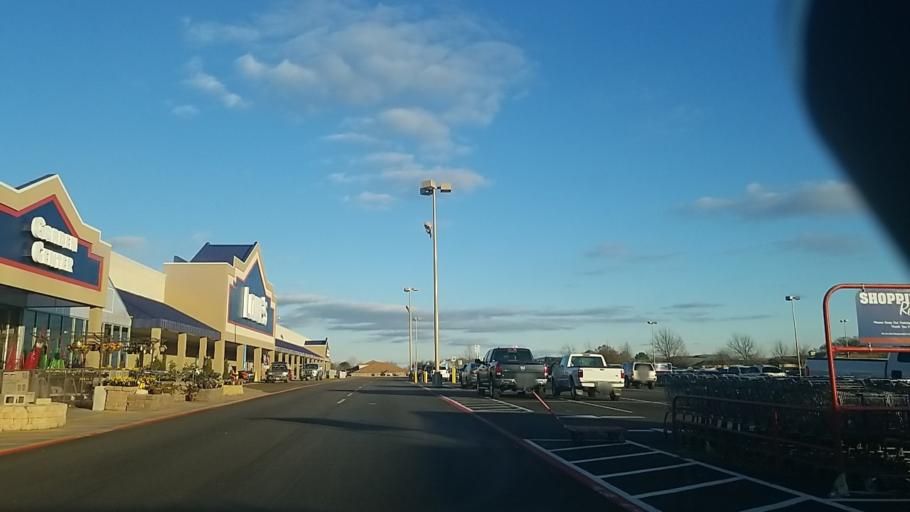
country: US
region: Texas
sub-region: Denton County
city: Denton
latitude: 33.1968
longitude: -97.0909
